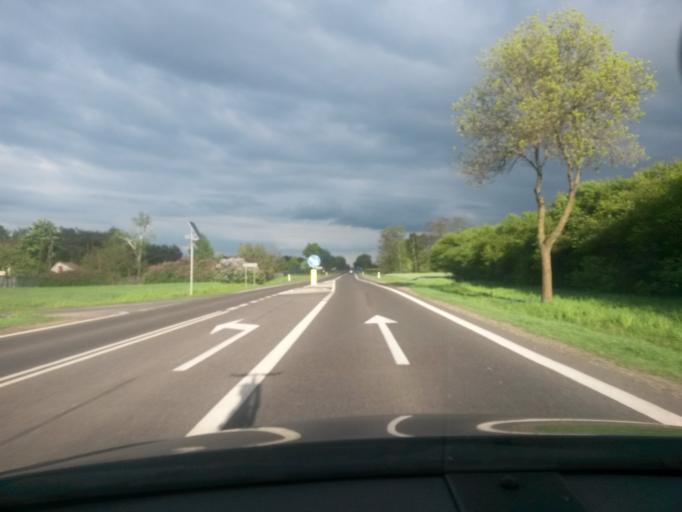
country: PL
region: Masovian Voivodeship
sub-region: Powiat plonski
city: Dzierzaznia
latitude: 52.6217
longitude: 20.2978
